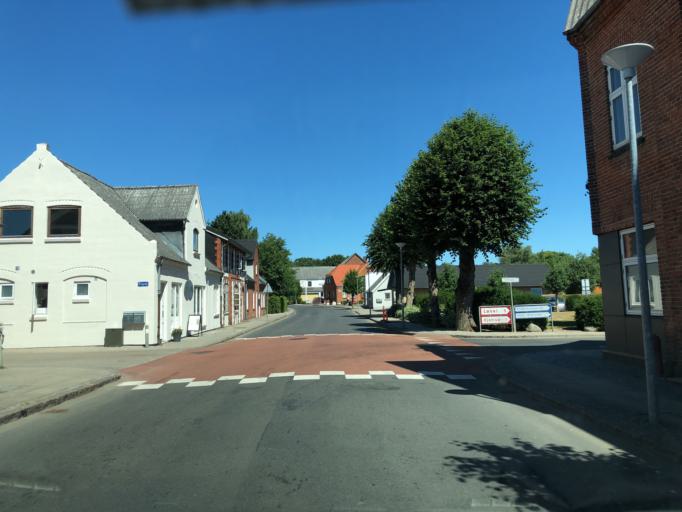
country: DK
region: Central Jutland
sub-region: Viborg Kommune
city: Viborg
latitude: 56.5577
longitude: 9.4035
